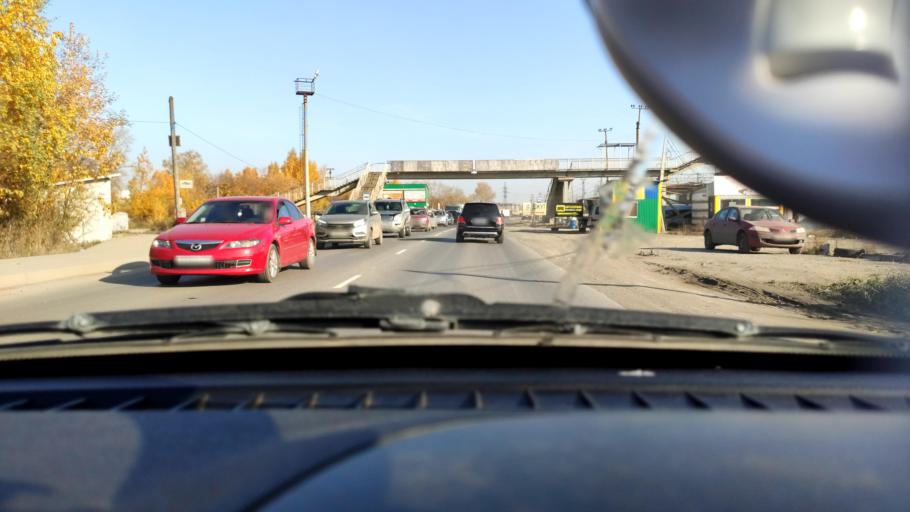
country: RU
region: Perm
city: Froly
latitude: 57.9537
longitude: 56.2344
